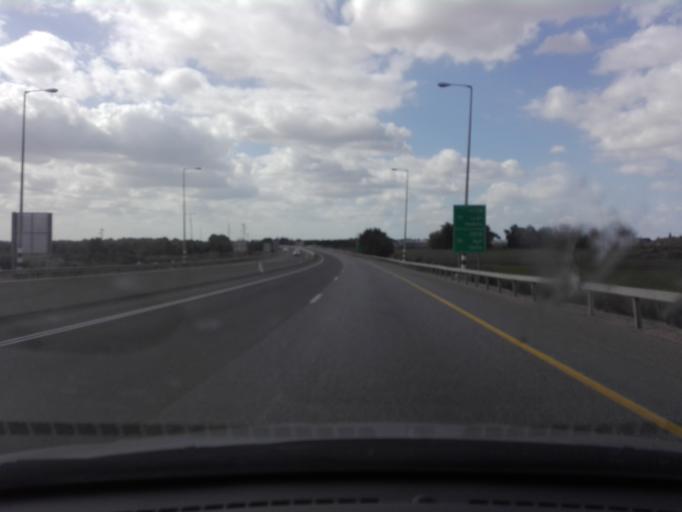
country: PS
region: West Bank
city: Barta`ah ash Sharqiyah
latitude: 32.4809
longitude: 35.0233
